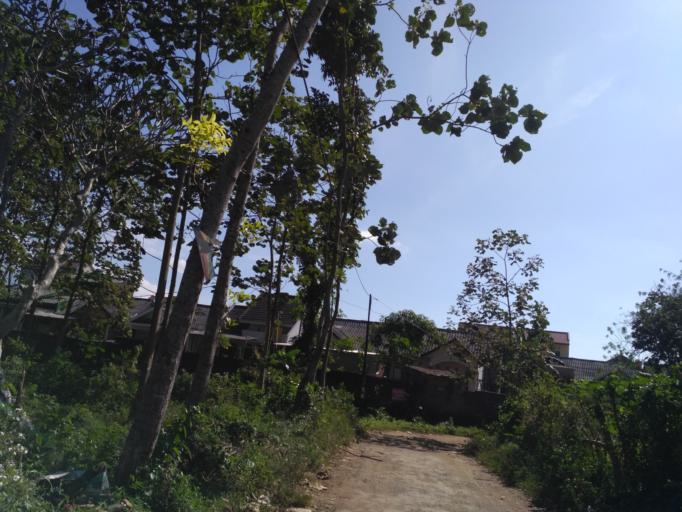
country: ID
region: East Java
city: Singosari
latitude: -7.9138
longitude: 112.6682
